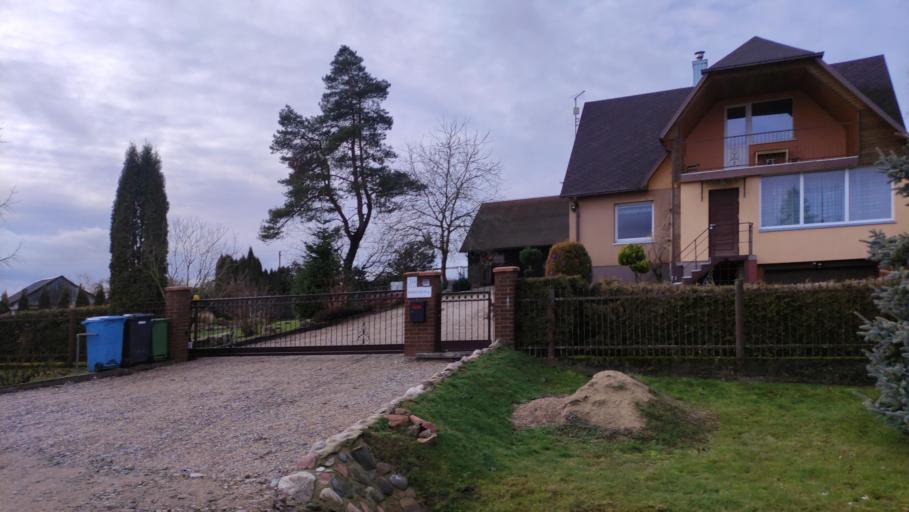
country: LT
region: Alytaus apskritis
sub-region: Alytus
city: Alytus
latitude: 54.3799
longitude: 23.9667
